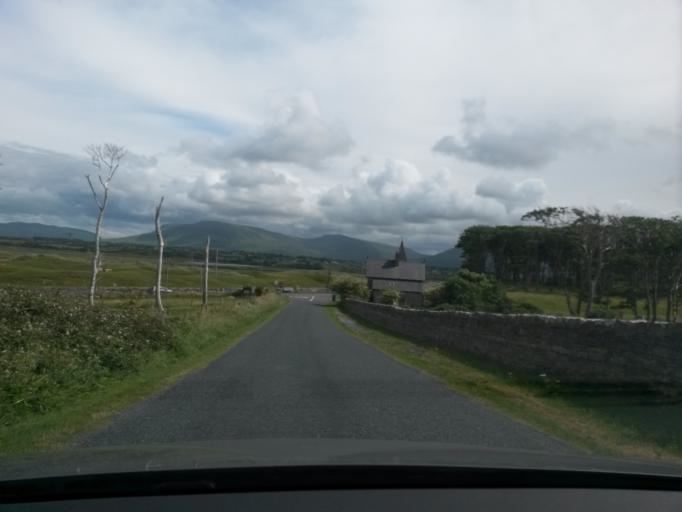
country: IE
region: Connaught
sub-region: County Leitrim
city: Kinlough
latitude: 54.4583
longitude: -8.4570
